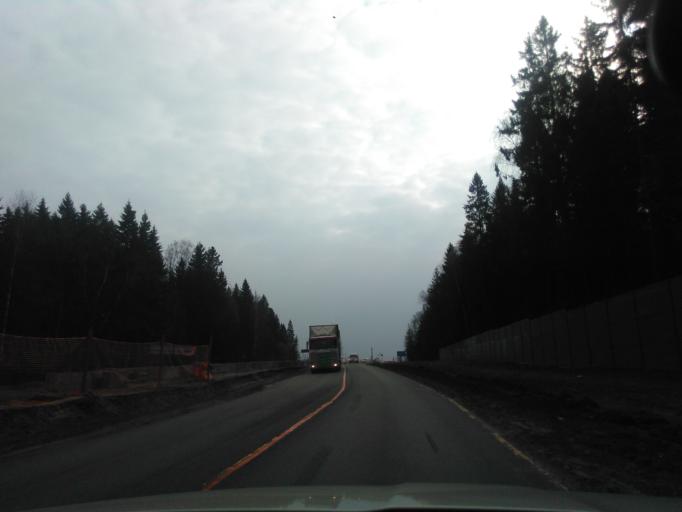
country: RU
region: Moskovskaya
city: Yermolino
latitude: 56.1380
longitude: 37.4826
